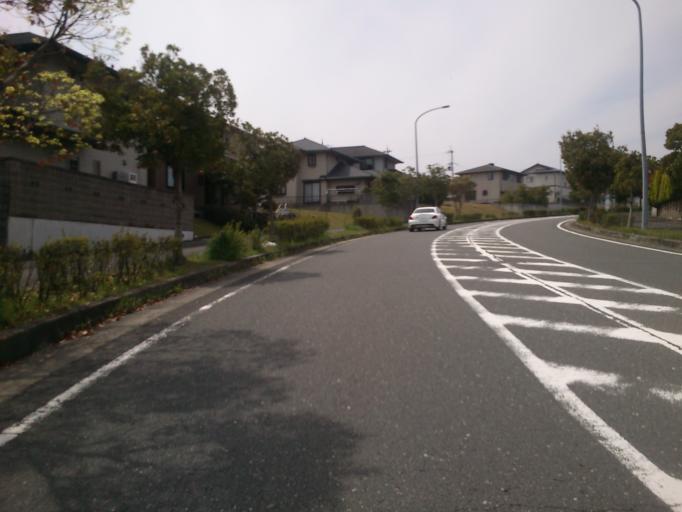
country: JP
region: Nara
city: Nara-shi
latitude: 34.7247
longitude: 135.8007
